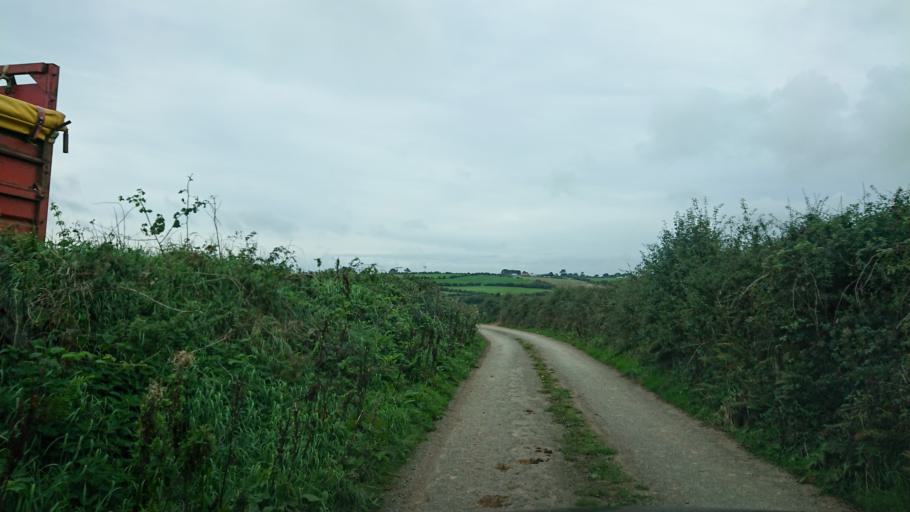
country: IE
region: Munster
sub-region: Waterford
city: Dunmore East
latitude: 52.1748
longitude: -6.9943
